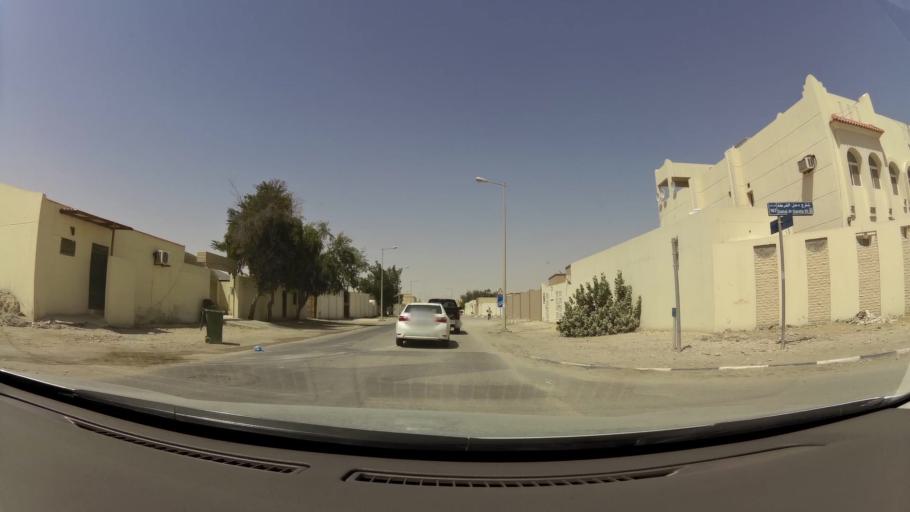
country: QA
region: Baladiyat ar Rayyan
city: Ar Rayyan
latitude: 25.2630
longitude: 51.4112
